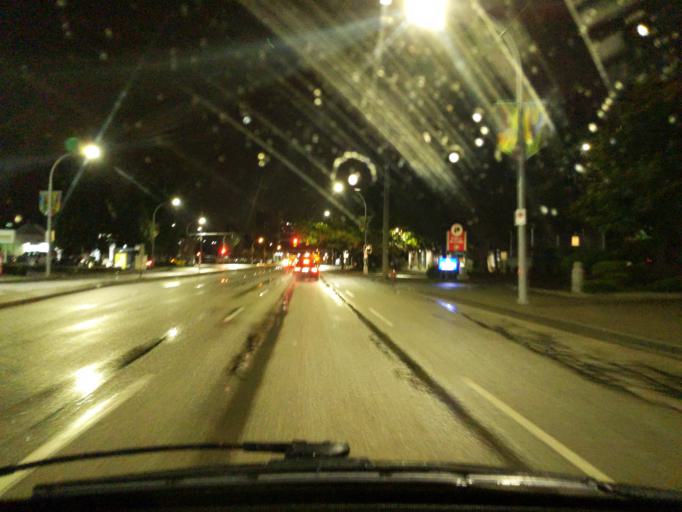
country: CA
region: British Columbia
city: Surrey
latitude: 49.1916
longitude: -122.7990
